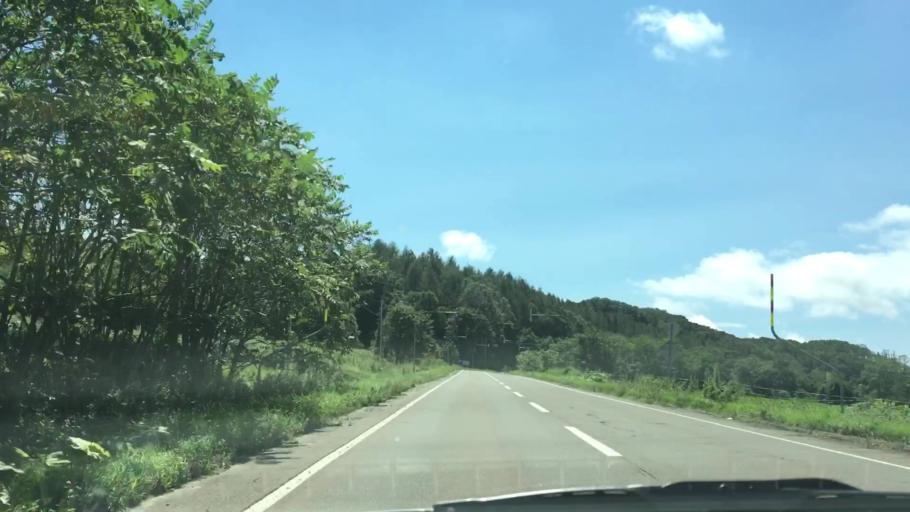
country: JP
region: Hokkaido
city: Kitami
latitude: 43.3187
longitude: 143.7221
